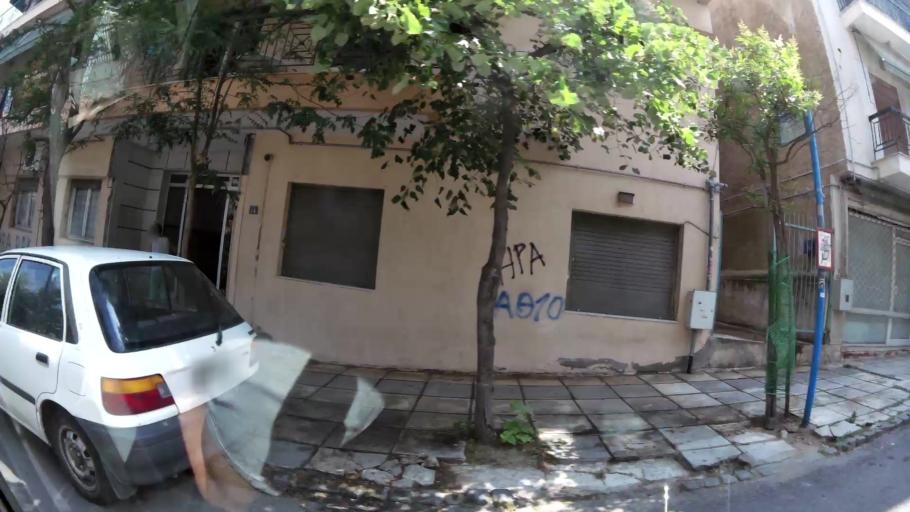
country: GR
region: Central Macedonia
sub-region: Nomos Thessalonikis
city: Agios Pavlos
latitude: 40.6333
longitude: 22.9675
